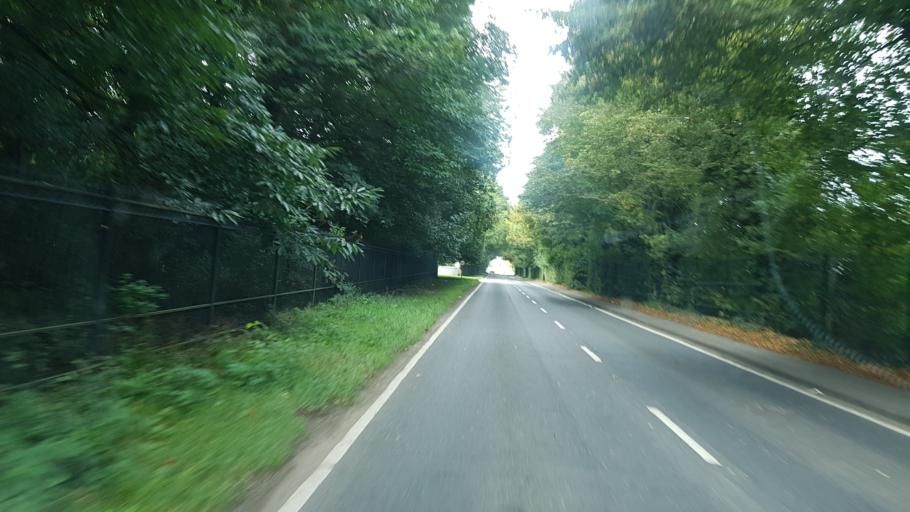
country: GB
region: England
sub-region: Kent
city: Maidstone
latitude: 51.2297
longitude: 0.5170
